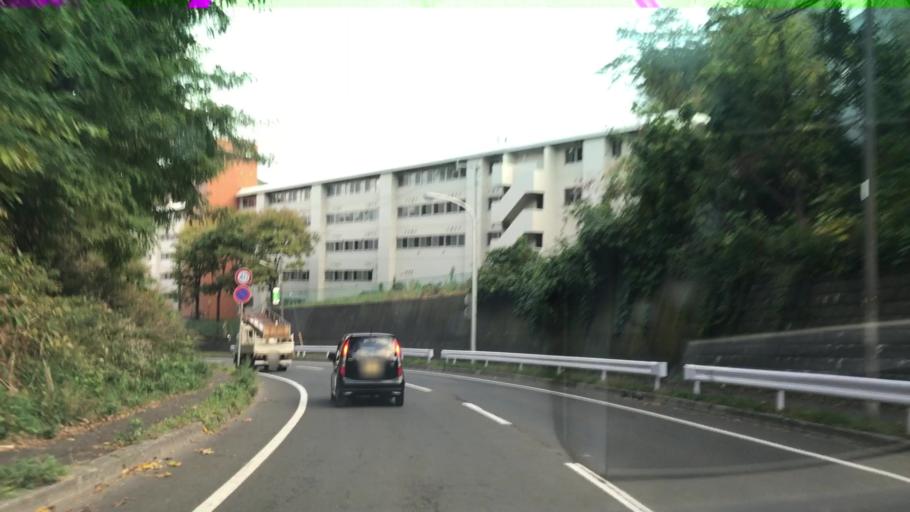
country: JP
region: Hokkaido
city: Sapporo
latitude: 43.0498
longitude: 141.3005
